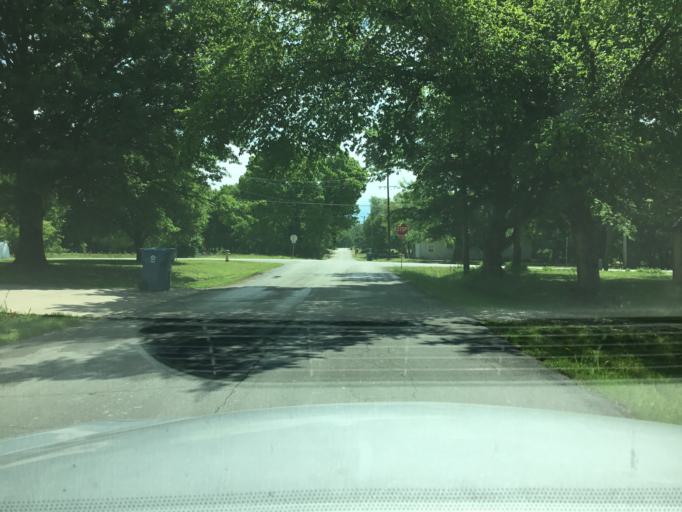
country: US
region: Kansas
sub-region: Montgomery County
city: Coffeyville
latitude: 37.0544
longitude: -95.6388
